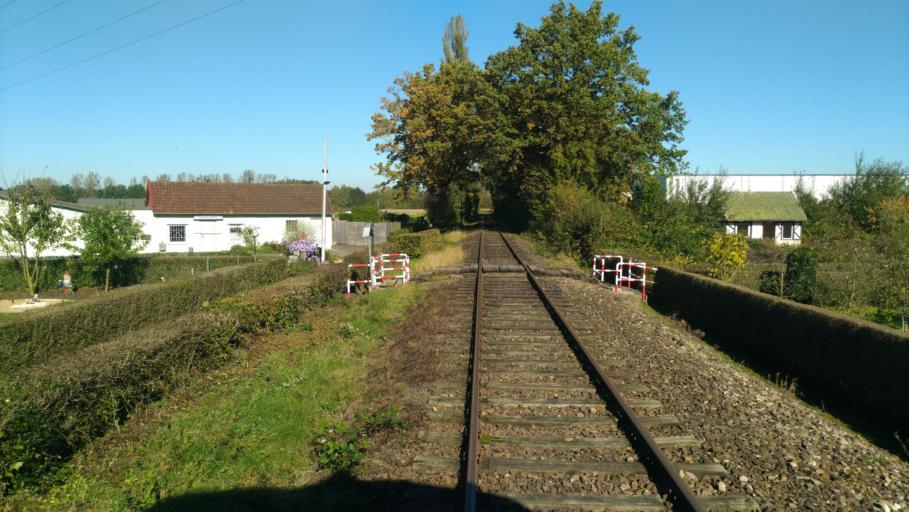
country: DE
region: Lower Saxony
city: Stadthagen
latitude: 52.3248
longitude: 9.1780
